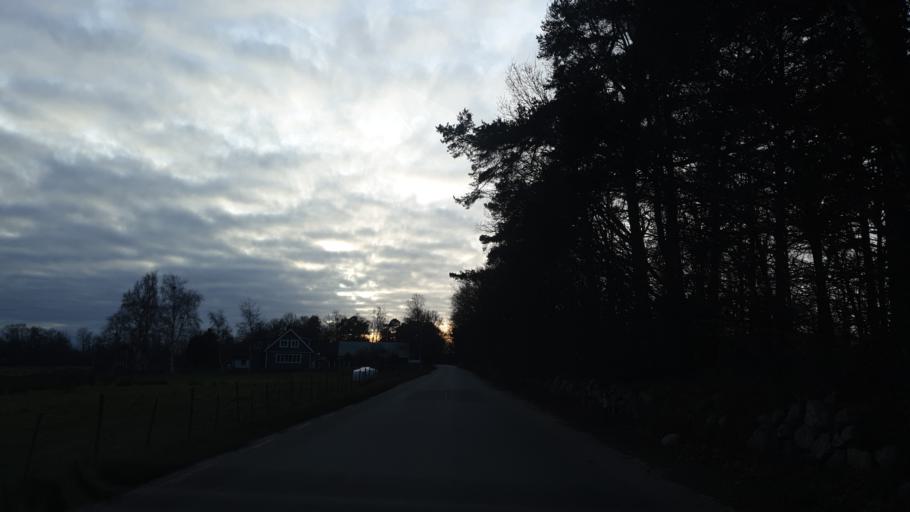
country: SE
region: Blekinge
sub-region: Karlskrona Kommun
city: Jaemjoe
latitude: 56.1618
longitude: 15.9171
